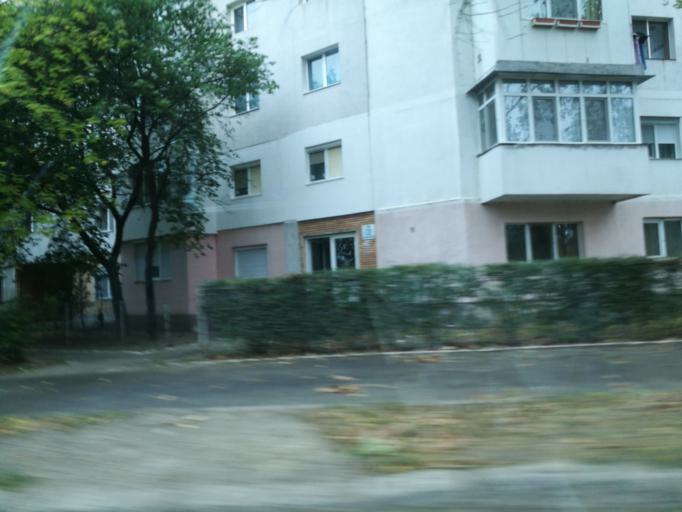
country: RO
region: Galati
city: Galati
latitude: 45.4571
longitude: 28.0174
